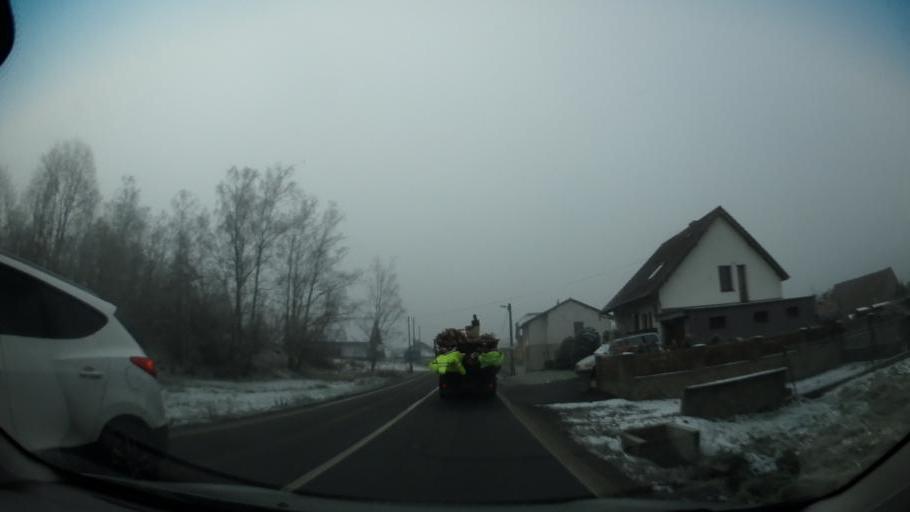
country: CZ
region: Vysocina
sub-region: Okres Trebic
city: Trebic
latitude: 49.2432
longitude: 15.8991
